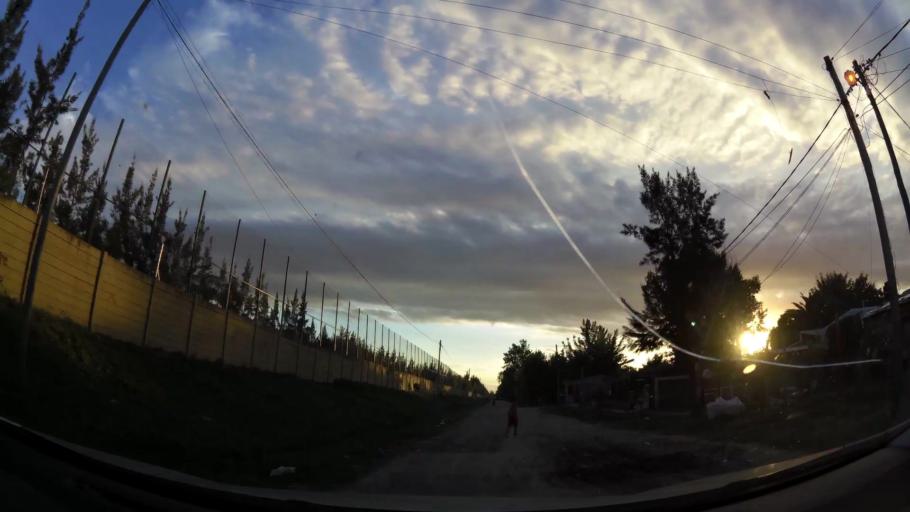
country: AR
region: Buenos Aires
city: Santa Catalina - Dique Lujan
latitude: -34.4311
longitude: -58.6604
